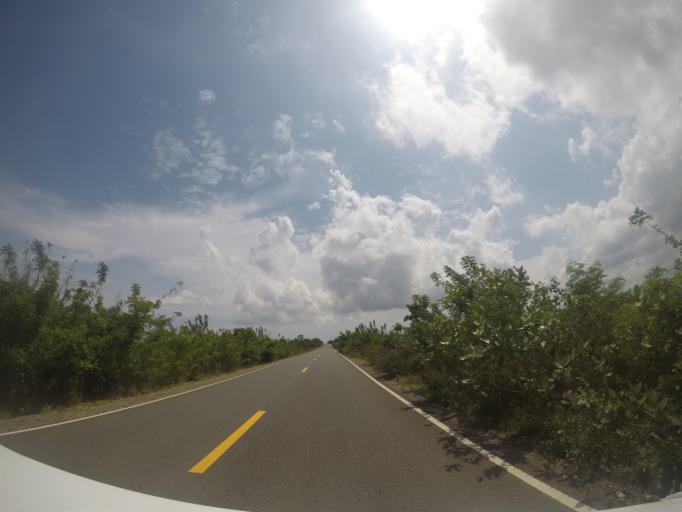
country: TL
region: Baucau
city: Baucau
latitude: -8.4855
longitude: 126.3803
